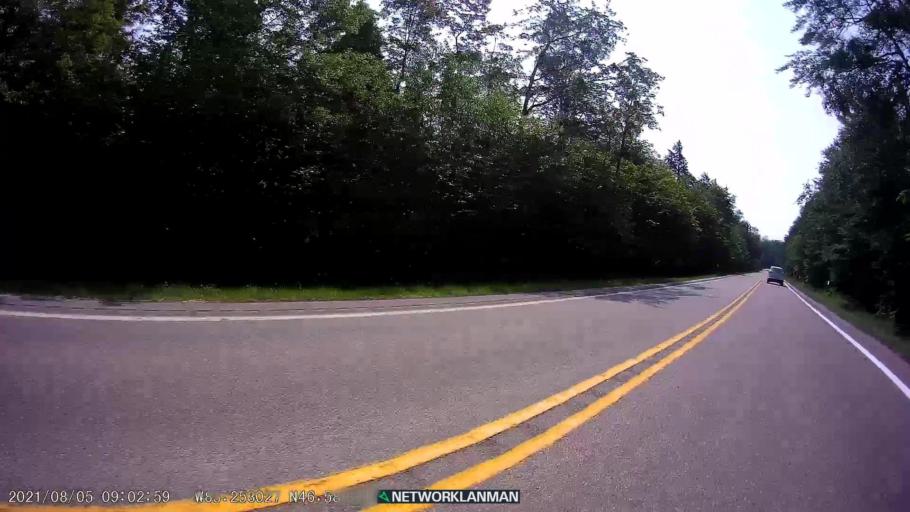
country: US
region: Michigan
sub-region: Luce County
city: Newberry
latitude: 46.5890
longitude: -85.2528
